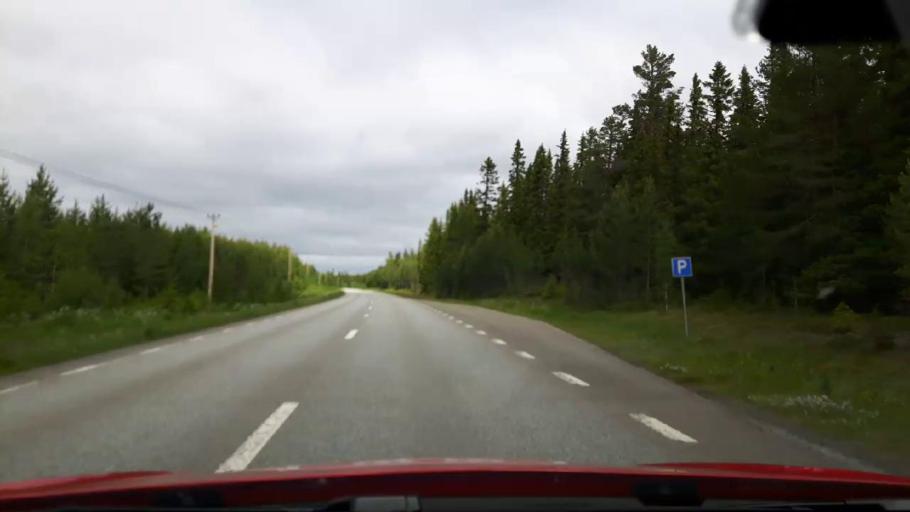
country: SE
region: Jaemtland
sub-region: Krokoms Kommun
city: Krokom
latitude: 63.4788
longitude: 14.5047
